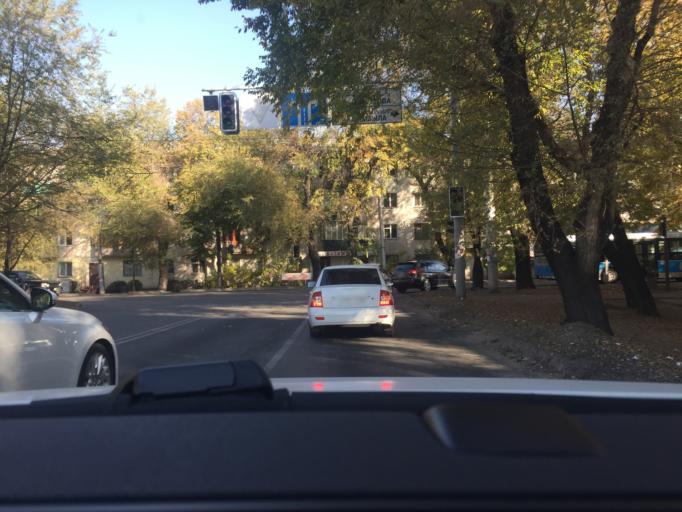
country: KZ
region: Almaty Qalasy
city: Almaty
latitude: 43.2450
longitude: 76.9079
